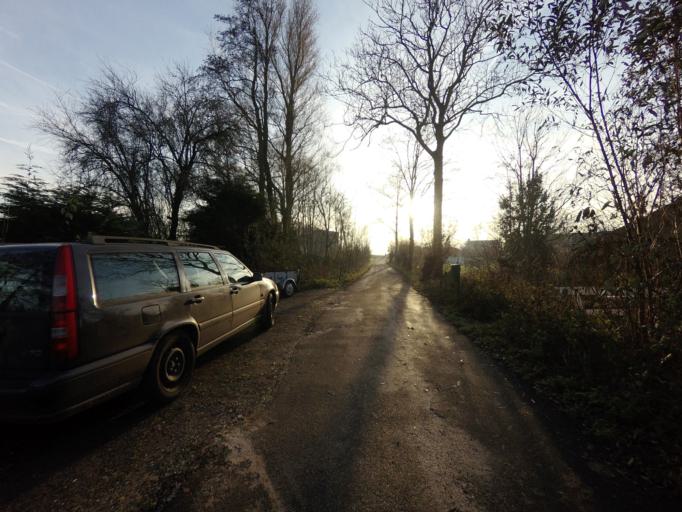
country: NL
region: Utrecht
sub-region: Stichtse Vecht
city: Breukelen
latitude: 52.1690
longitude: 4.9298
